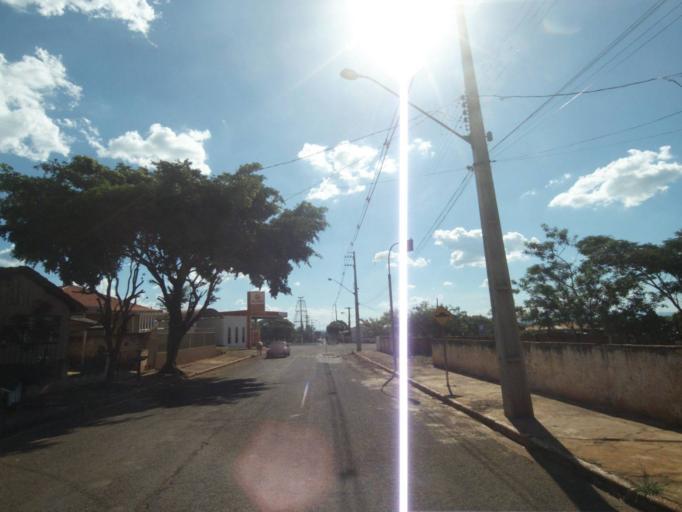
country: BR
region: Parana
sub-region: Sertanopolis
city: Sertanopolis
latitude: -23.0419
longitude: -50.8169
